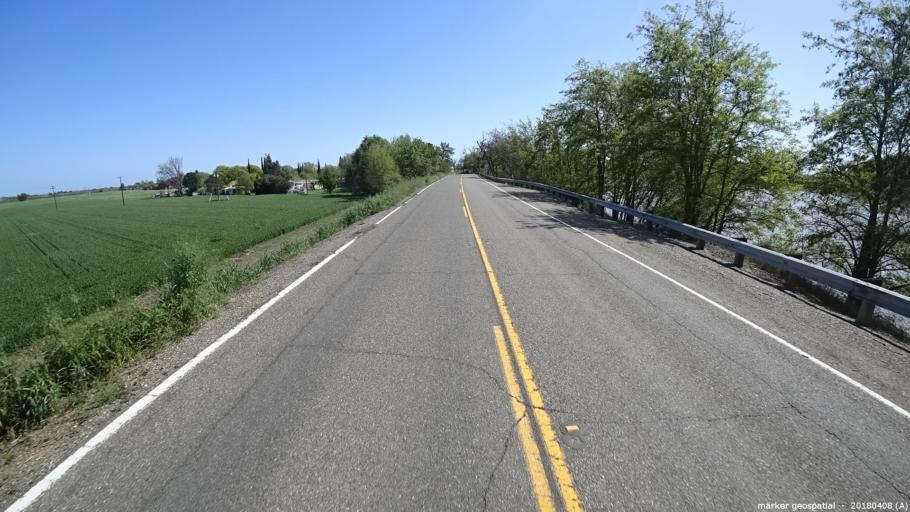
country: US
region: California
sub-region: Sacramento County
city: Laguna
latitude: 38.3715
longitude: -121.5212
